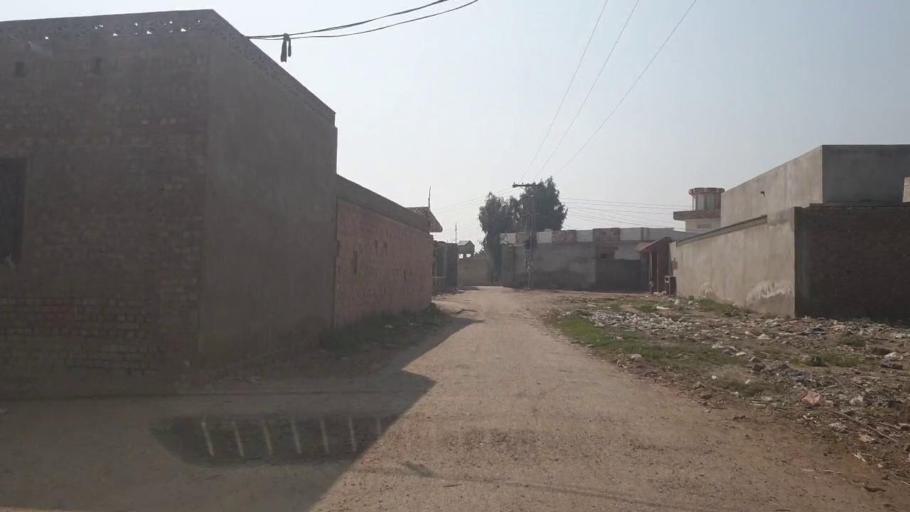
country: PK
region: Sindh
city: Tando Allahyar
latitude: 25.4792
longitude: 68.7910
